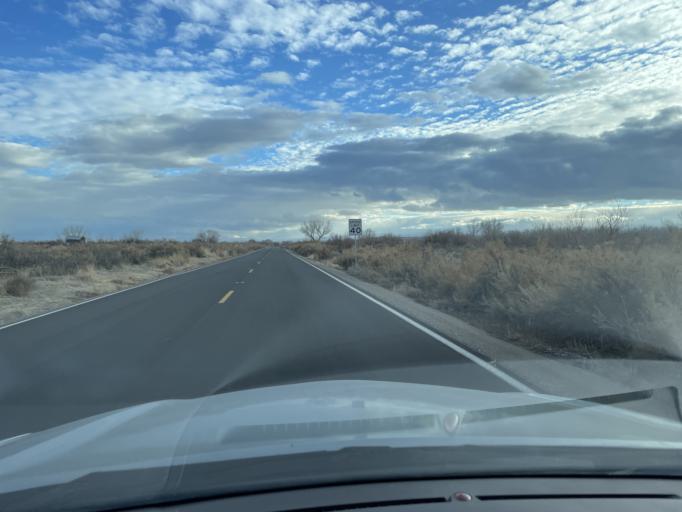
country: US
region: Colorado
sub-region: Montrose County
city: Olathe
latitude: 38.6490
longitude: -107.9952
